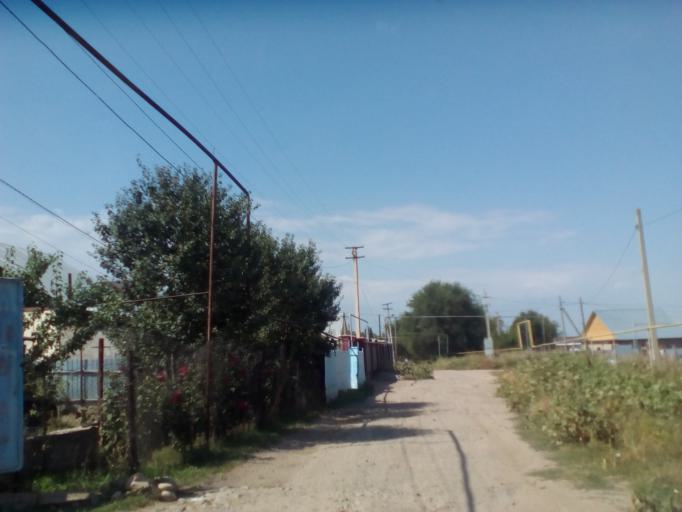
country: KZ
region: Almaty Oblysy
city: Burunday
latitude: 43.1595
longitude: 76.3989
